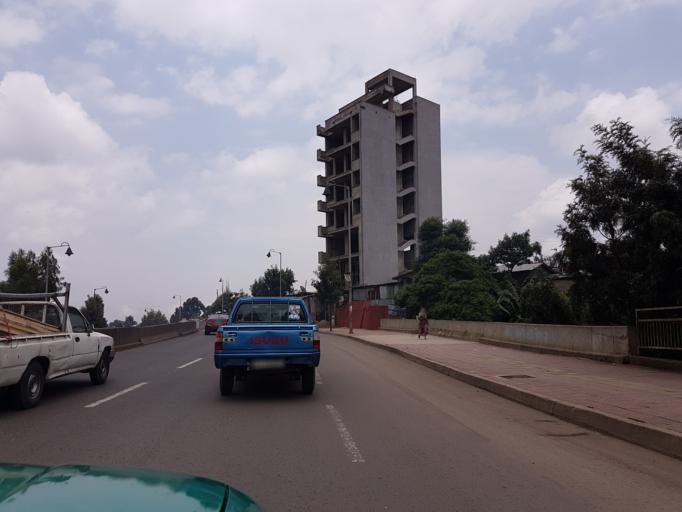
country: ET
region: Adis Abeba
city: Addis Ababa
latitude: 9.0067
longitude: 38.7339
